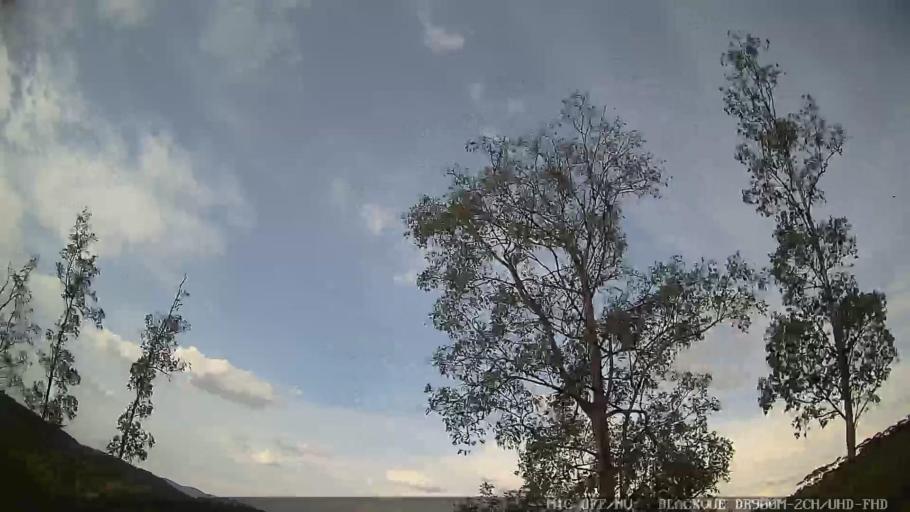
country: BR
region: Sao Paulo
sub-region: Amparo
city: Amparo
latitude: -22.7817
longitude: -46.7560
